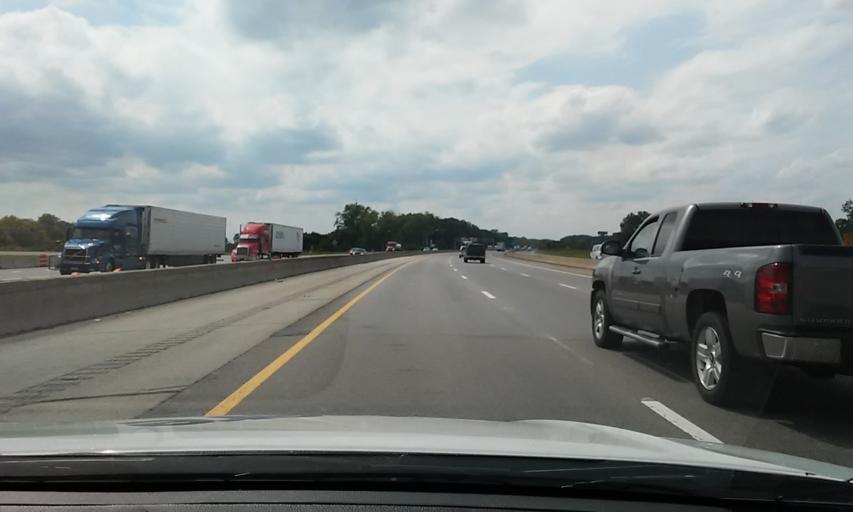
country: US
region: Ohio
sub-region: Clark County
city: Holiday Valley
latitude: 39.8654
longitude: -83.9942
